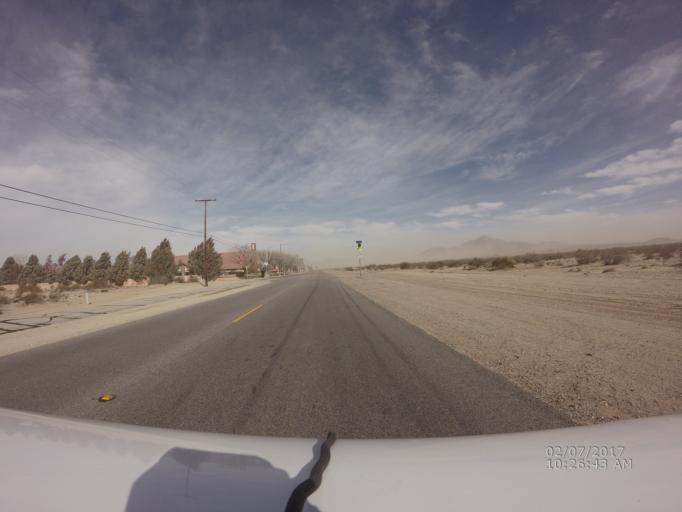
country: US
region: California
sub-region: Los Angeles County
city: Lake Los Angeles
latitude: 34.6368
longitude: -117.8272
